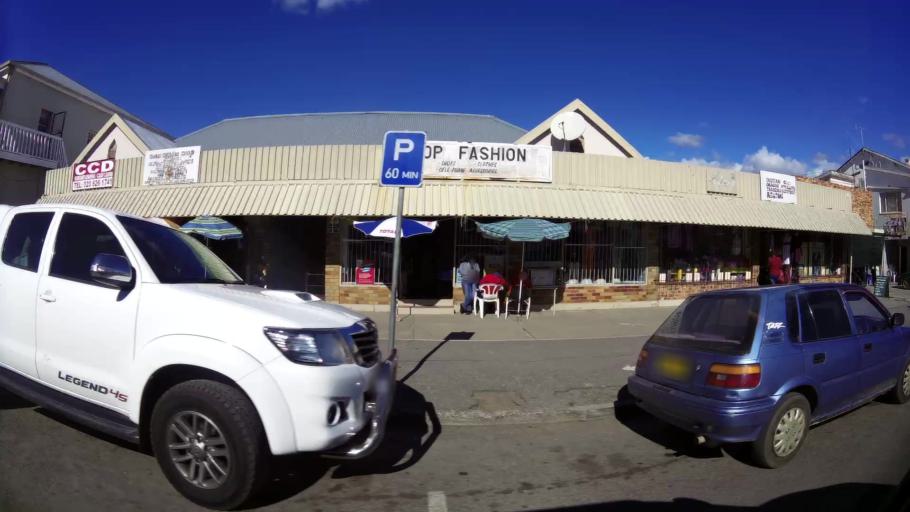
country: ZA
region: Western Cape
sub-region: Cape Winelands District Municipality
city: Ashton
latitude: -33.8059
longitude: 19.8834
